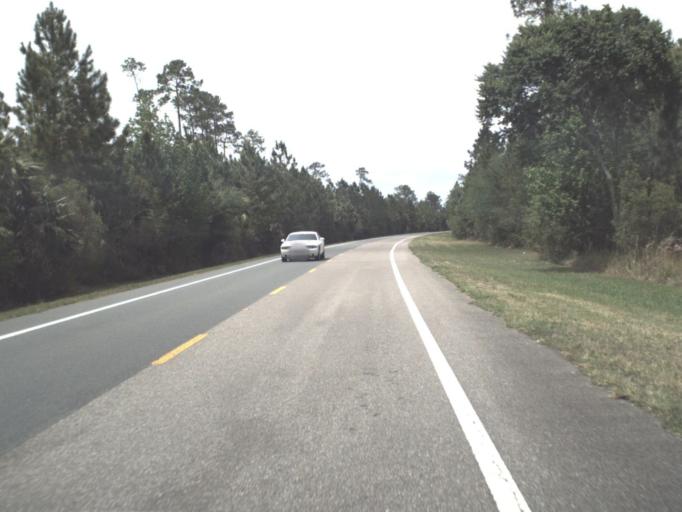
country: US
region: Florida
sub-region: Flagler County
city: Bunnell
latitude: 29.3698
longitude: -81.3118
